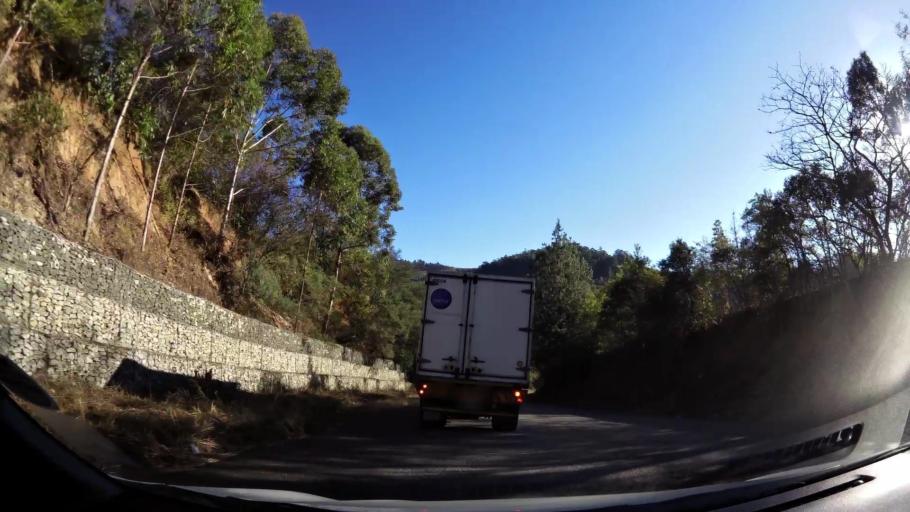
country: ZA
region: Limpopo
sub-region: Mopani District Municipality
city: Tzaneen
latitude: -23.9346
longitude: 30.0274
